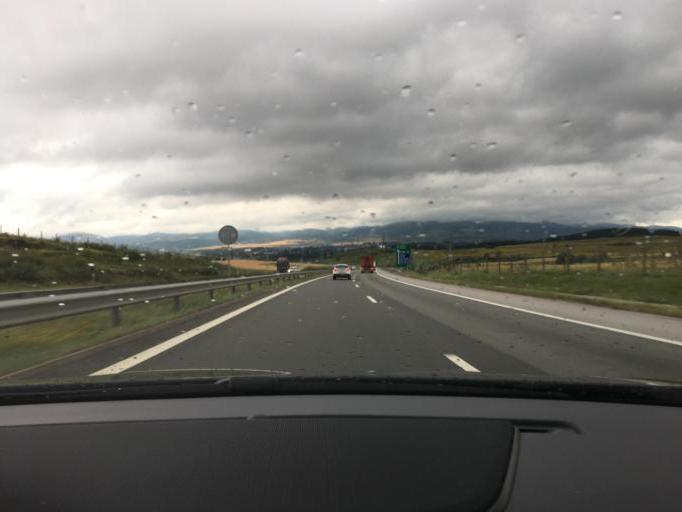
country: BG
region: Pernik
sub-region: Obshtina Pernik
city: Pernik
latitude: 42.6124
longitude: 23.1370
